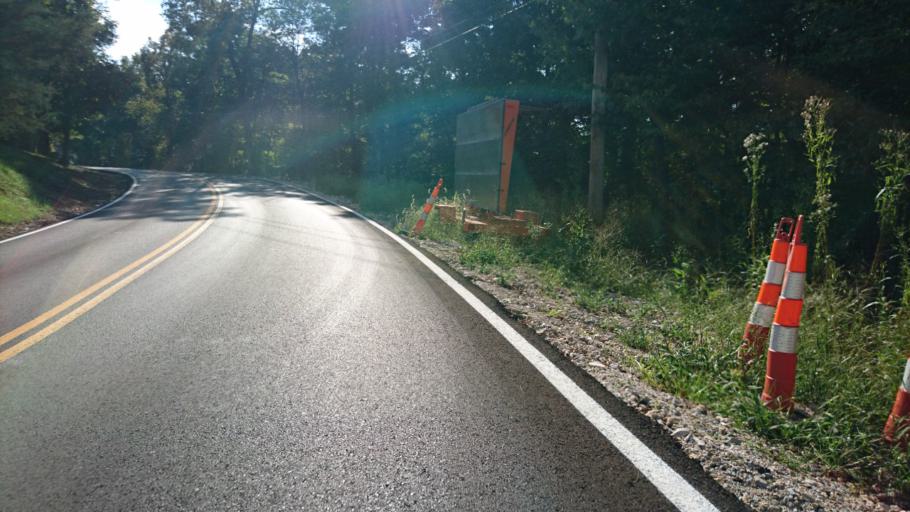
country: US
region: Missouri
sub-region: Saint Louis County
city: Eureka
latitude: 38.5402
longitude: -90.6350
